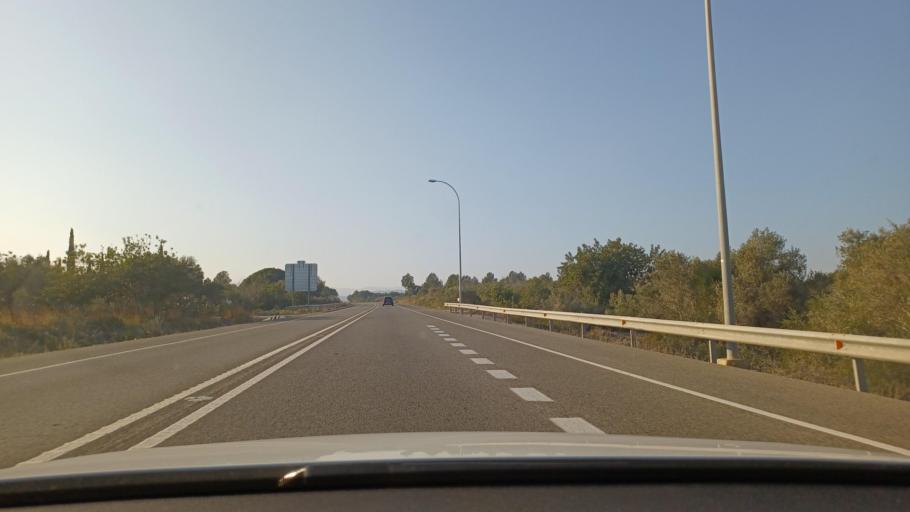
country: ES
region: Catalonia
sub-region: Provincia de Tarragona
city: l'Ametlla de Mar
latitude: 40.8936
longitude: 0.7774
